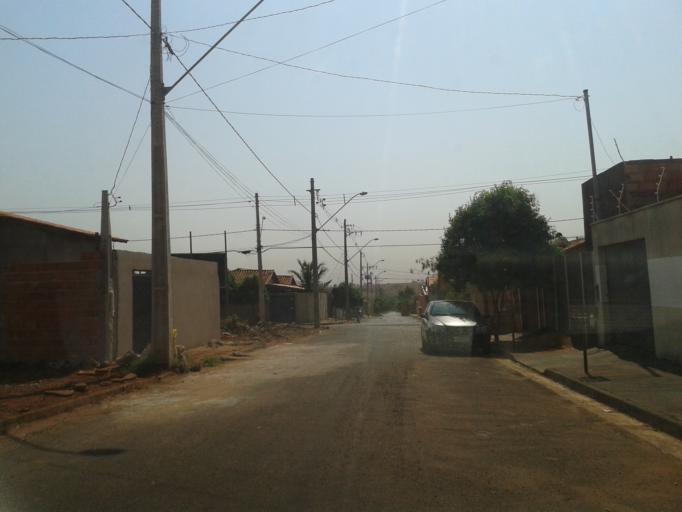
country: BR
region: Minas Gerais
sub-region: Ituiutaba
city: Ituiutaba
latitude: -18.9862
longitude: -49.4292
